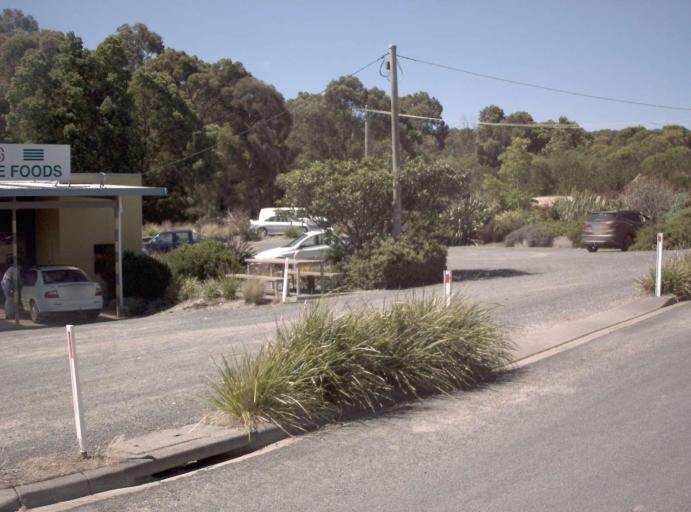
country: AU
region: Victoria
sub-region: Latrobe
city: Morwell
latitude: -38.6496
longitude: 146.2053
